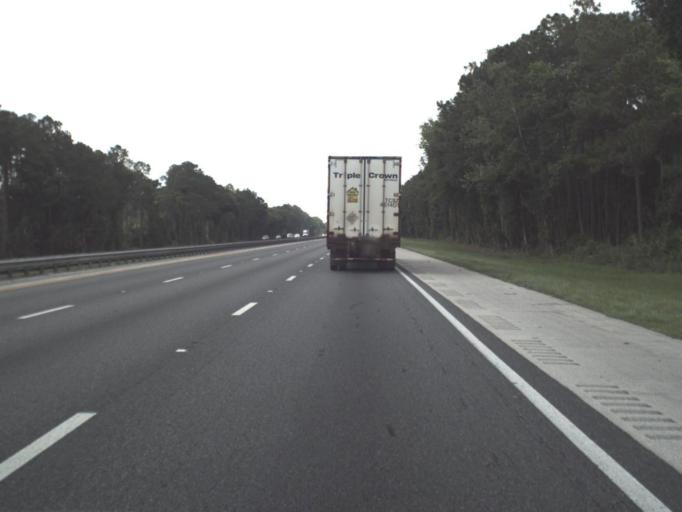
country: US
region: Florida
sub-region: Saint Johns County
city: Saint Augustine
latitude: 29.8821
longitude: -81.4011
